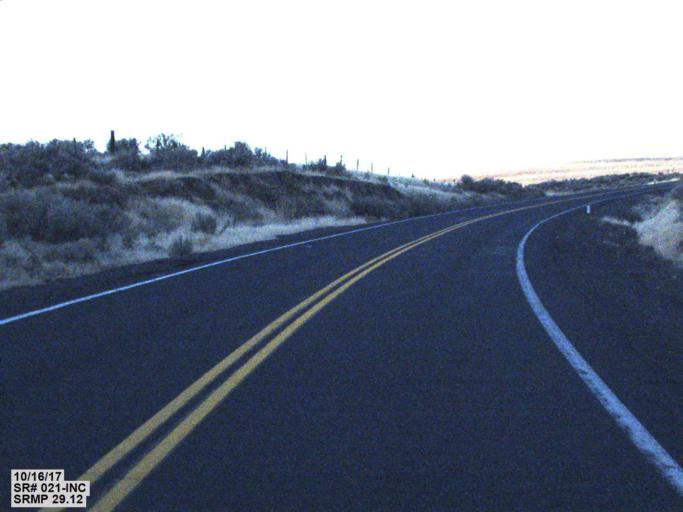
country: US
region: Washington
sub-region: Adams County
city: Ritzville
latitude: 46.9721
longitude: -118.6643
